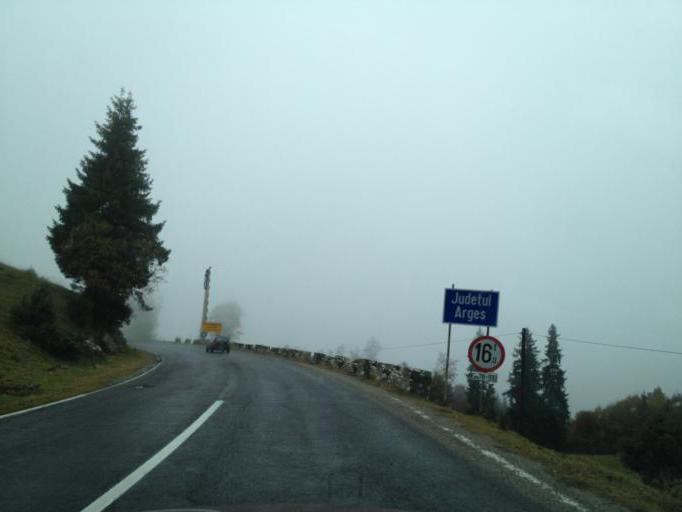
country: RO
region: Brasov
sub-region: Comuna Fundata
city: Fundata
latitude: 45.4389
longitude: 25.2668
